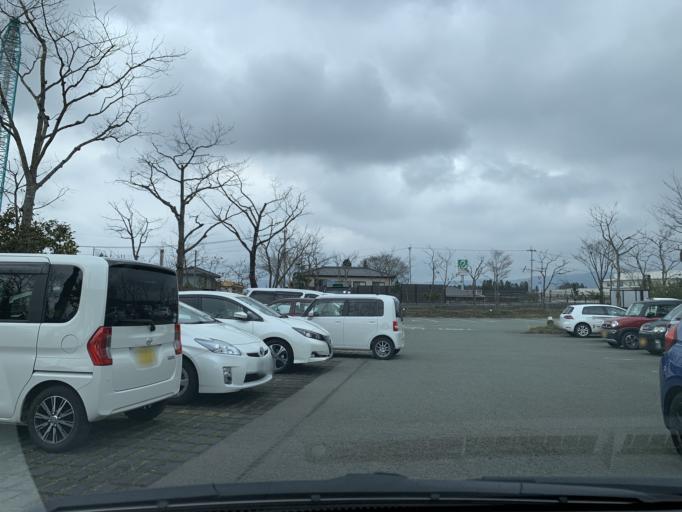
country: JP
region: Kumamoto
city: Aso
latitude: 32.9366
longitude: 131.0809
